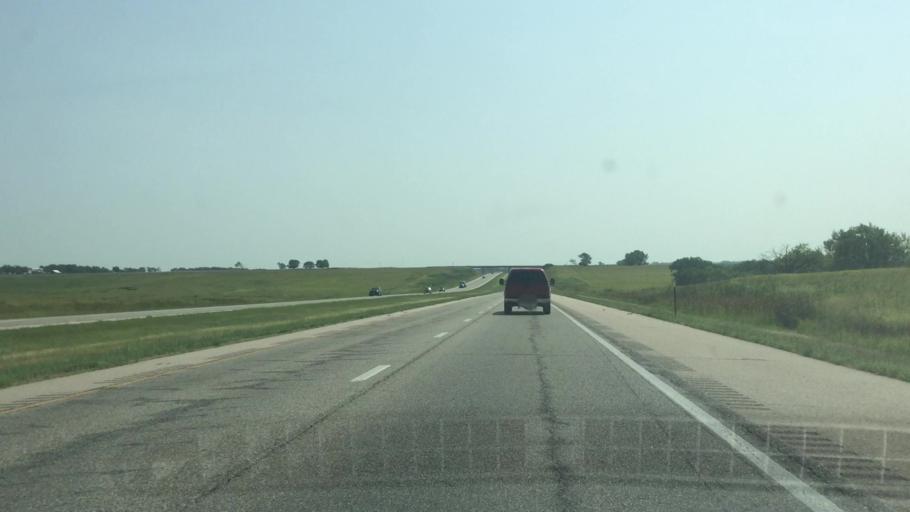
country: US
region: Kansas
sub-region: Osage County
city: Osage City
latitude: 38.4260
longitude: -95.7960
